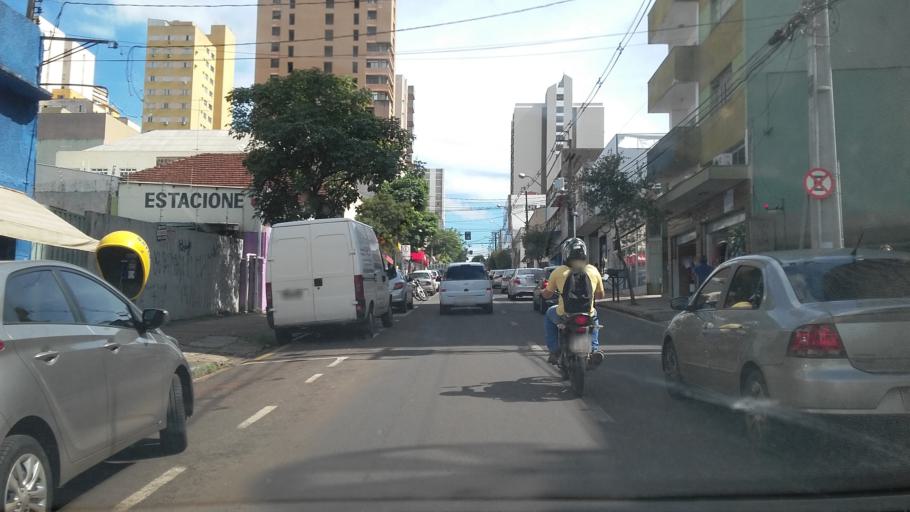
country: BR
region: Parana
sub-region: Londrina
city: Londrina
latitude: -23.3089
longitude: -51.1628
